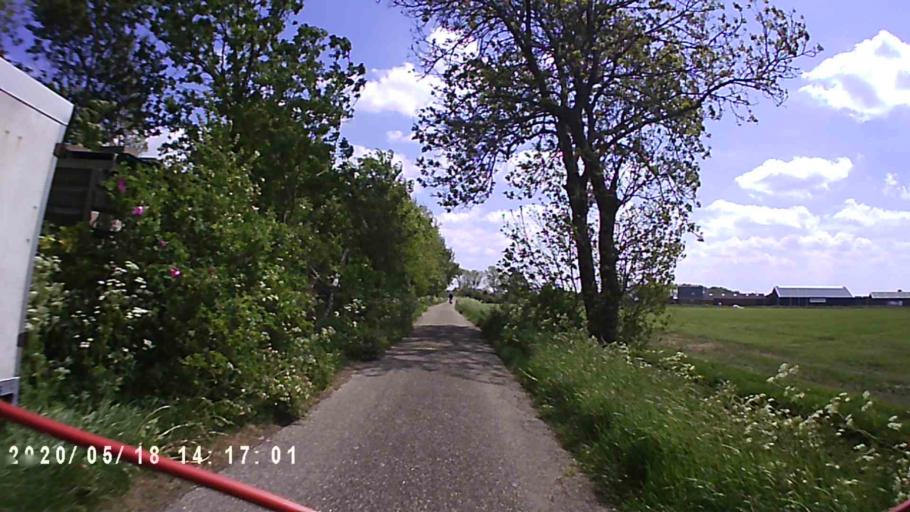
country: NL
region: Groningen
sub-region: Gemeente Winsum
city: Winsum
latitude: 53.3084
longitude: 6.4768
